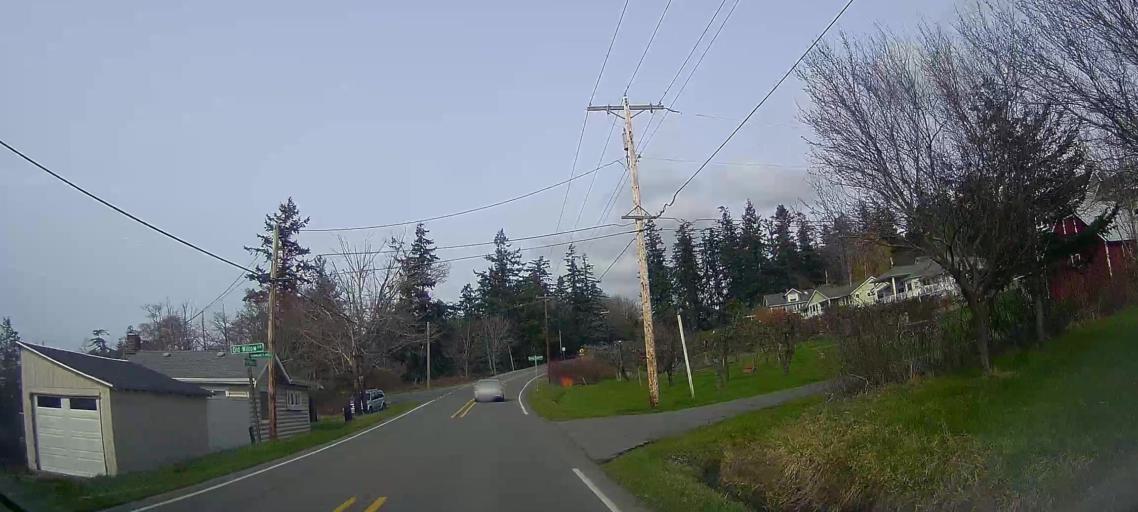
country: US
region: Washington
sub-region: Island County
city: Camano
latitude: 48.1735
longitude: -122.5286
